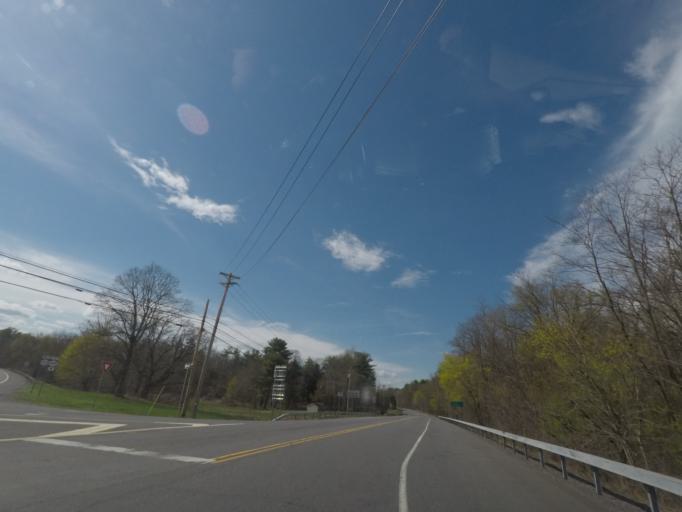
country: US
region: New York
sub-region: Greene County
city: Cairo
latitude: 42.3081
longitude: -74.0045
